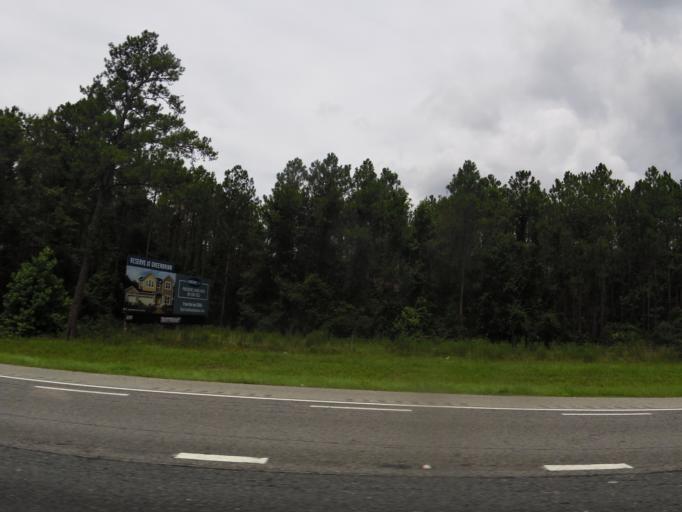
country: US
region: Florida
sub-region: Saint Johns County
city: Fruit Cove
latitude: 30.0807
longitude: -81.4985
